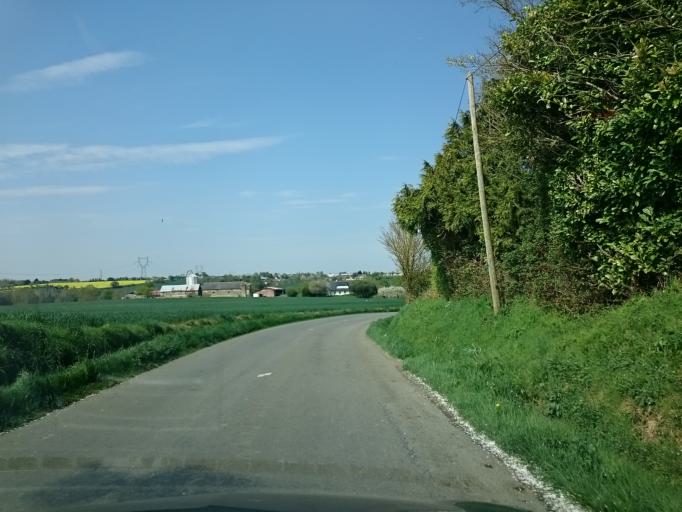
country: FR
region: Brittany
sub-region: Departement d'Ille-et-Vilaine
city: Nouvoitou
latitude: 48.0479
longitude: -1.5308
